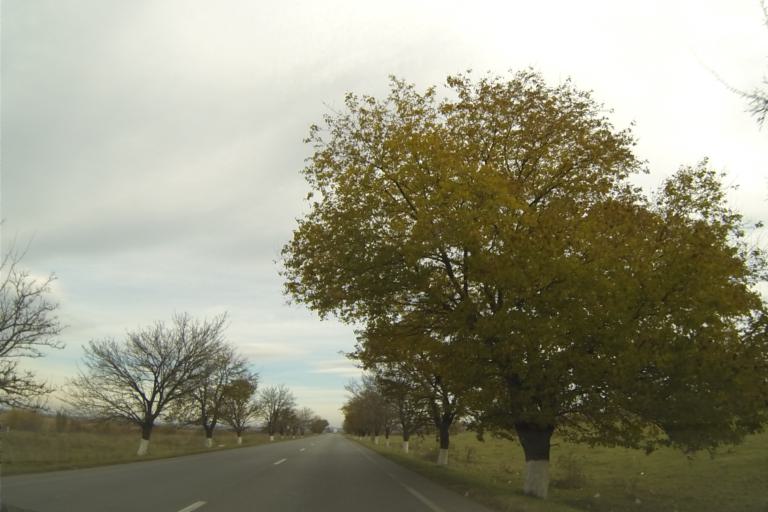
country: RO
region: Olt
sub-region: Comuna Ganeasa
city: Ganeasa
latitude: 44.4055
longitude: 24.2974
